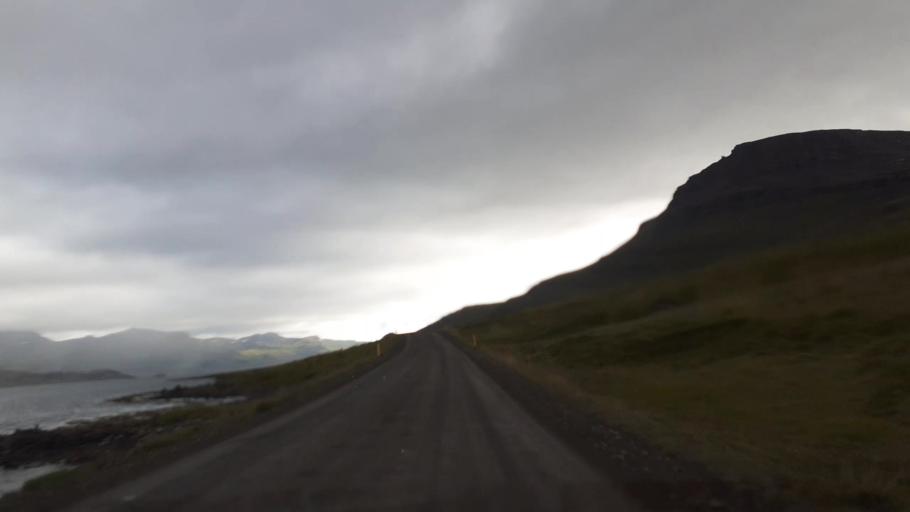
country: IS
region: East
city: Reydarfjoerdur
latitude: 65.0131
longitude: -14.1599
